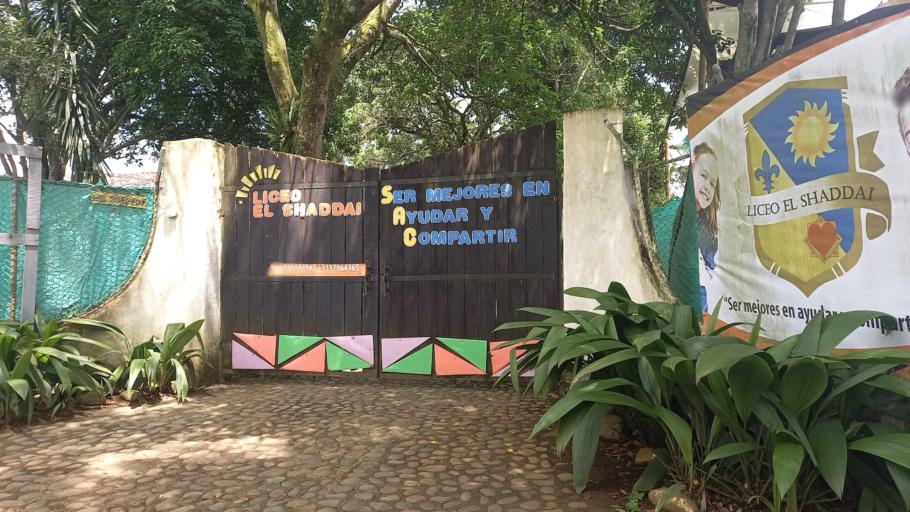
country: CO
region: Valle del Cauca
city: Jamundi
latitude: 3.2347
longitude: -76.5824
